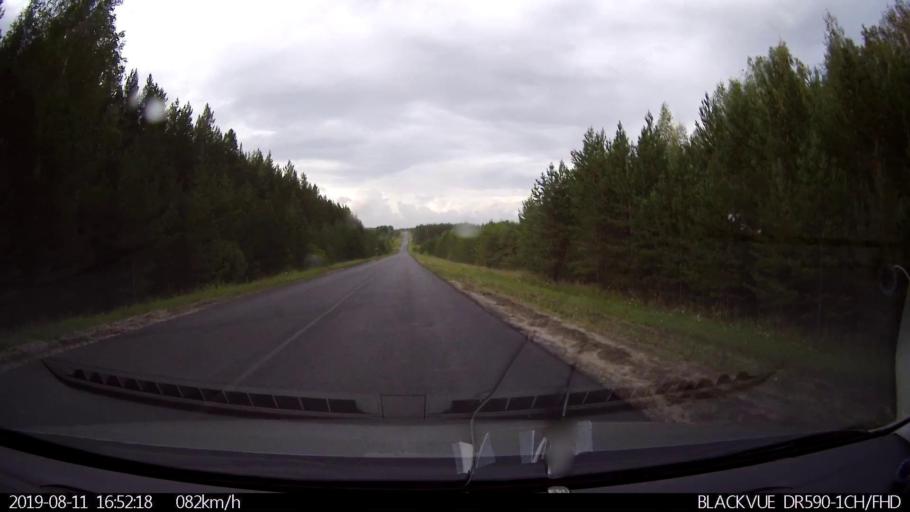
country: RU
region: Ulyanovsk
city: Mayna
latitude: 54.2464
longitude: 47.6746
